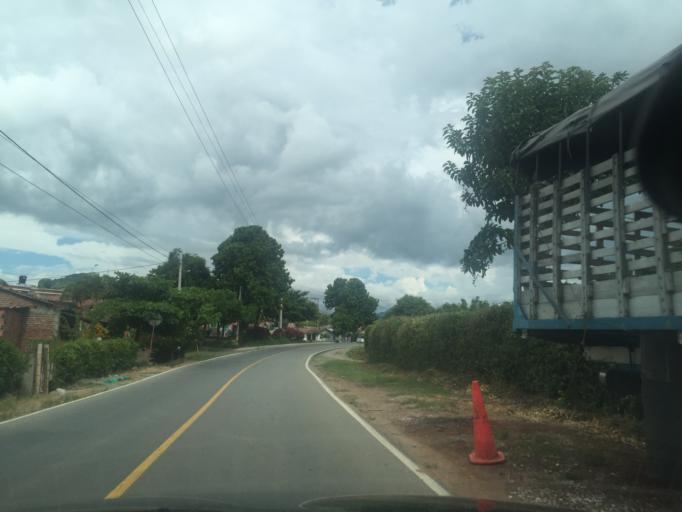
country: CO
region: Valle del Cauca
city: Caicedonia
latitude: 4.3426
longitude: -75.8519
